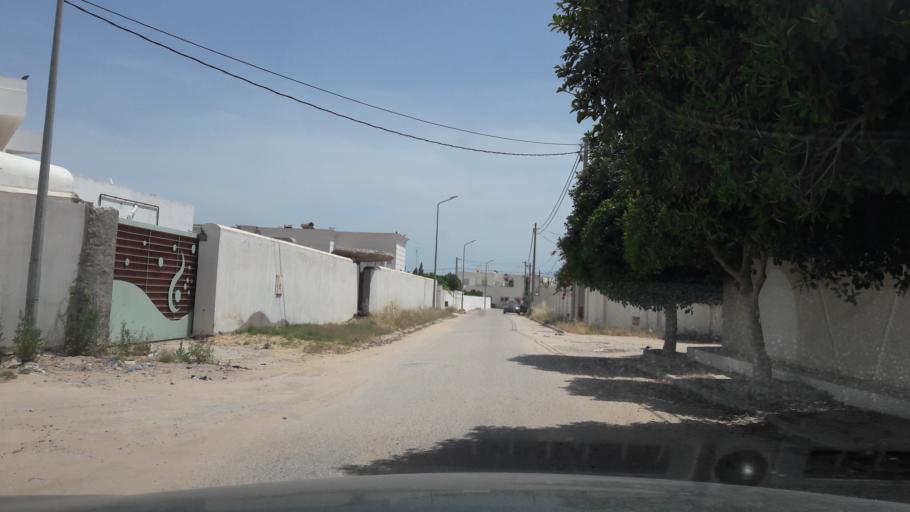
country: TN
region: Safaqis
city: Sfax
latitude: 34.7756
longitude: 10.7573
